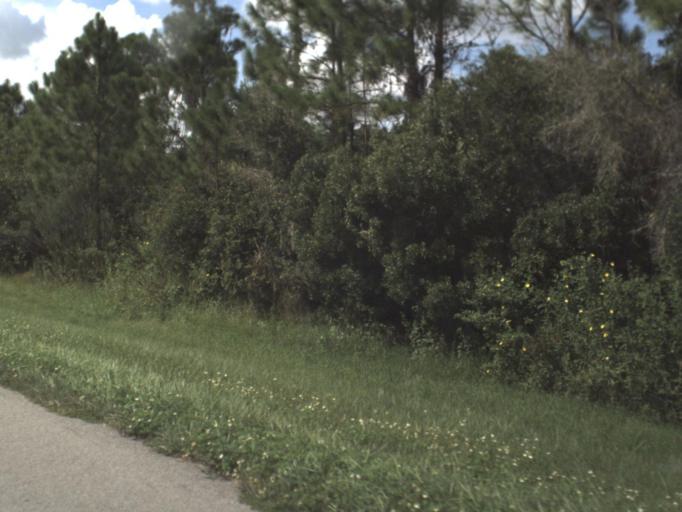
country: US
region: Florida
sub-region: Hillsborough County
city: Wimauma
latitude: 27.4703
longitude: -82.2004
